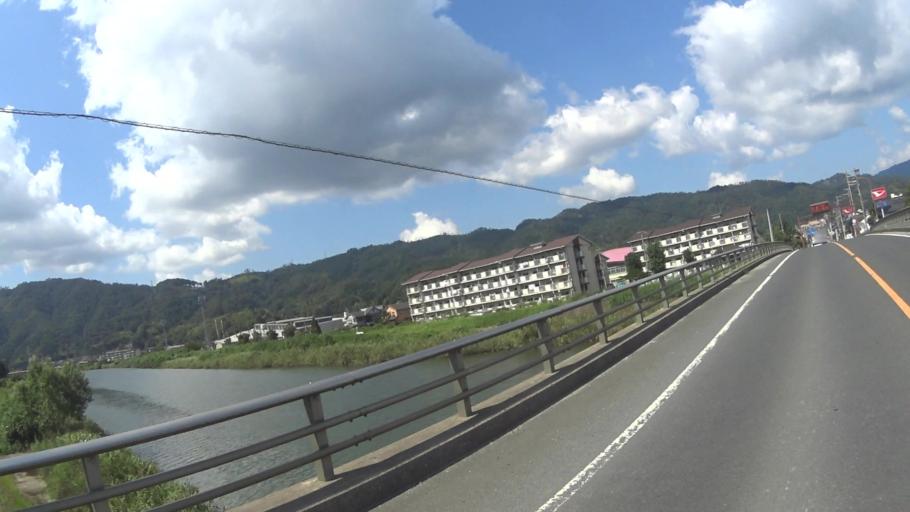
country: JP
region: Kyoto
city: Miyazu
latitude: 35.5595
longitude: 135.1536
